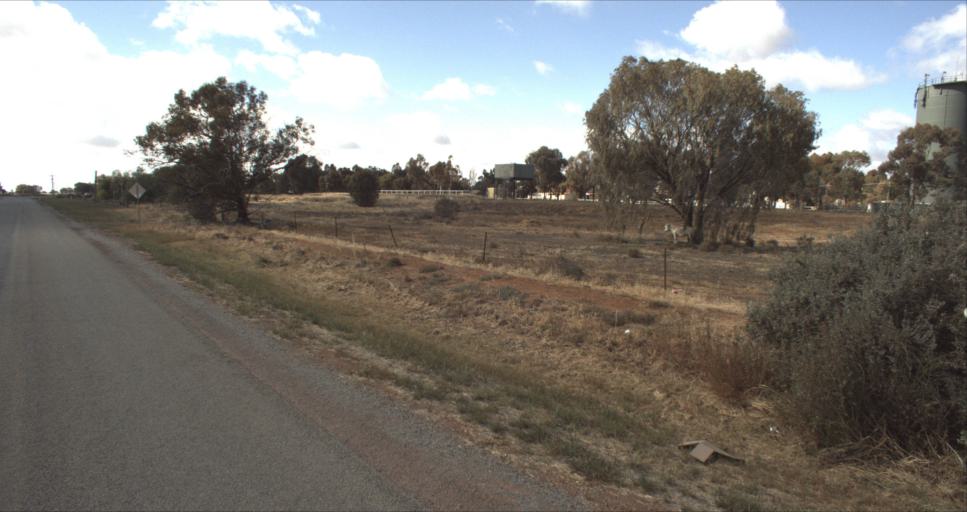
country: AU
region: New South Wales
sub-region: Murrumbidgee Shire
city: Darlington Point
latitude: -34.5155
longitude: 146.1826
